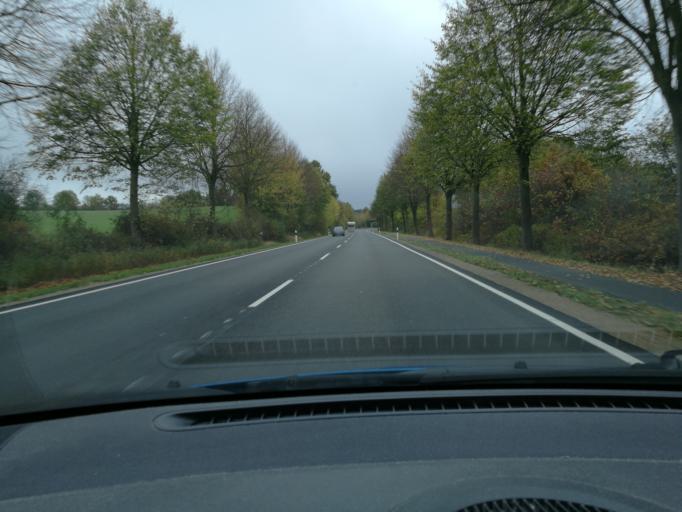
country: DE
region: Schleswig-Holstein
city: Fredeburg
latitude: 53.6816
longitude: 10.7292
